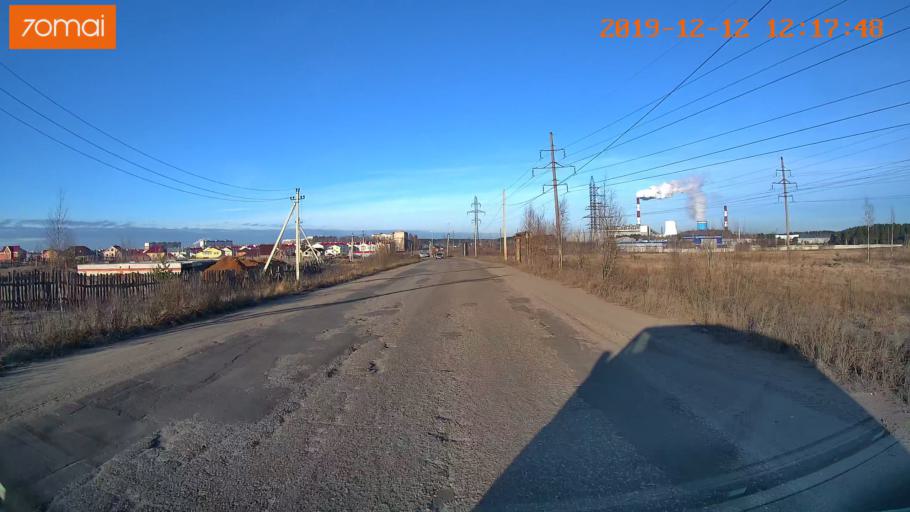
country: RU
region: Ivanovo
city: Kokhma
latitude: 56.9457
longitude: 41.1121
